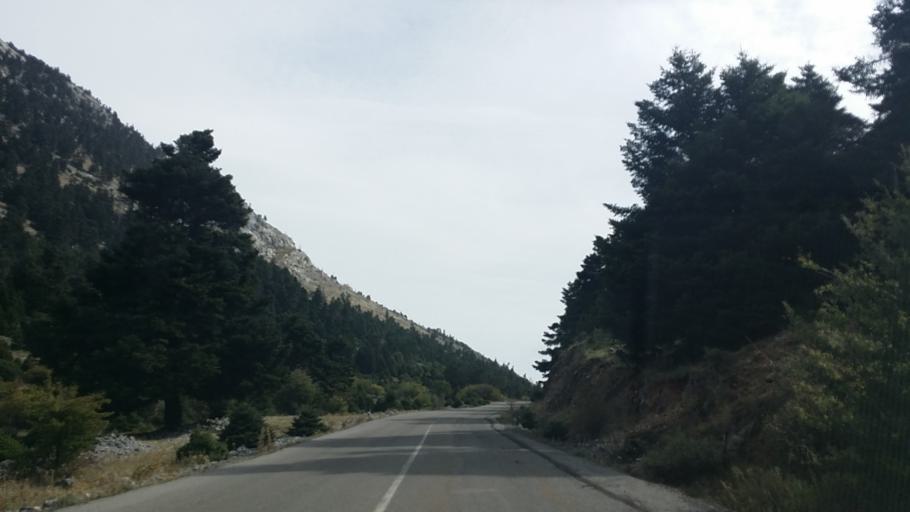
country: GR
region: Central Greece
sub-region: Nomos Voiotias
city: Kyriaki
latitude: 38.3333
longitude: 22.8366
